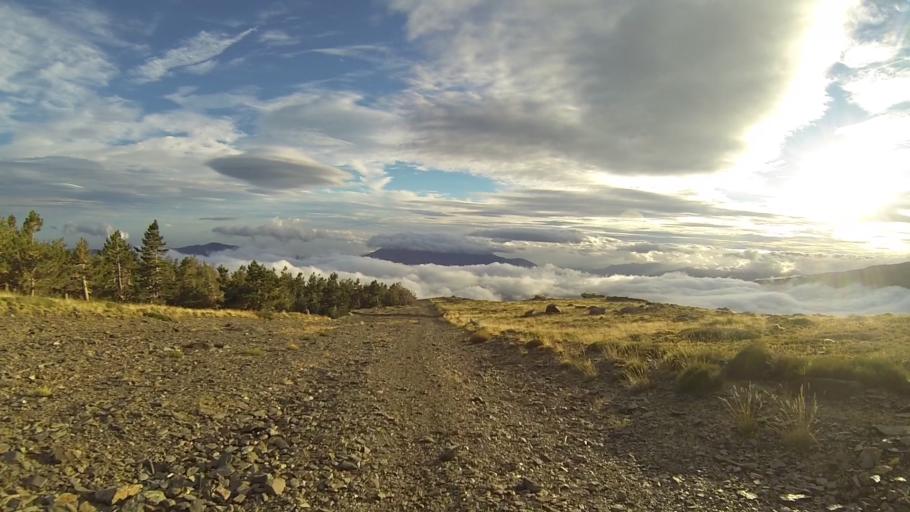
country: ES
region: Andalusia
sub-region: Provincia de Granada
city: Capileira
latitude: 36.9753
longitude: -3.3331
